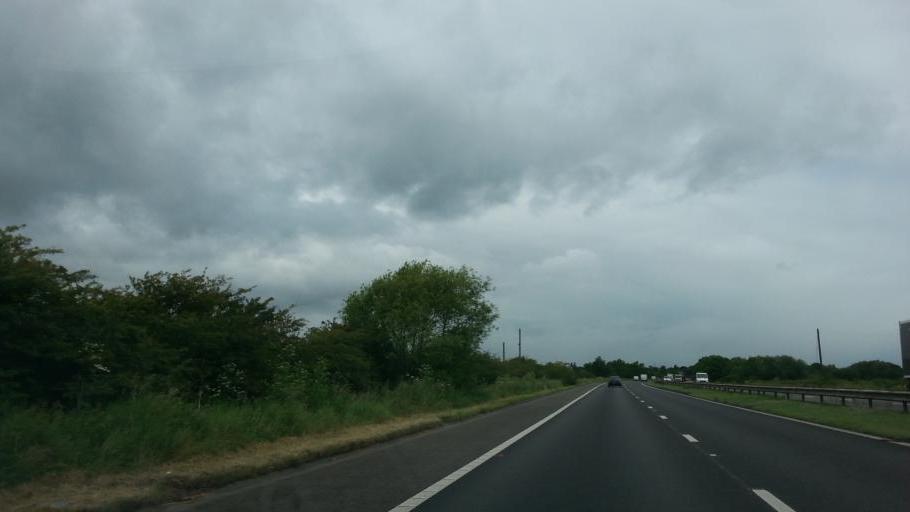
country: GB
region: England
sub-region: Doncaster
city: Tickhill
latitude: 53.4195
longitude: -1.0890
